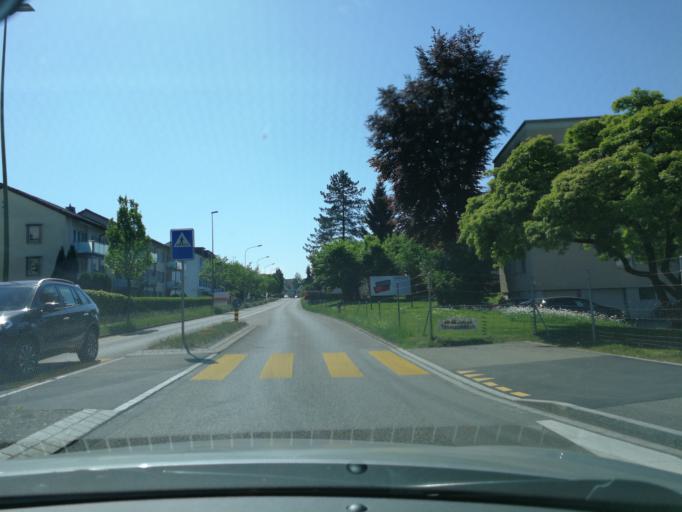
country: CH
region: Zurich
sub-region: Bezirk Hinwil
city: Hinwil
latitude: 47.2985
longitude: 8.8378
